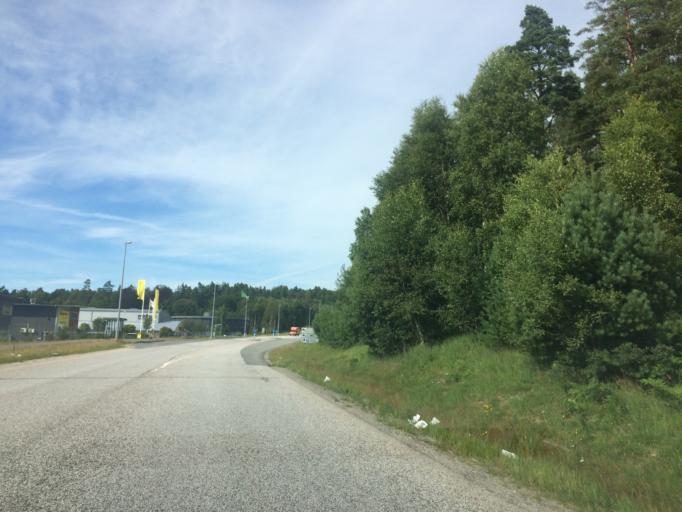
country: SE
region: Vaestra Goetaland
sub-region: Harryda Kommun
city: Molnlycke
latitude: 57.6781
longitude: 12.0945
